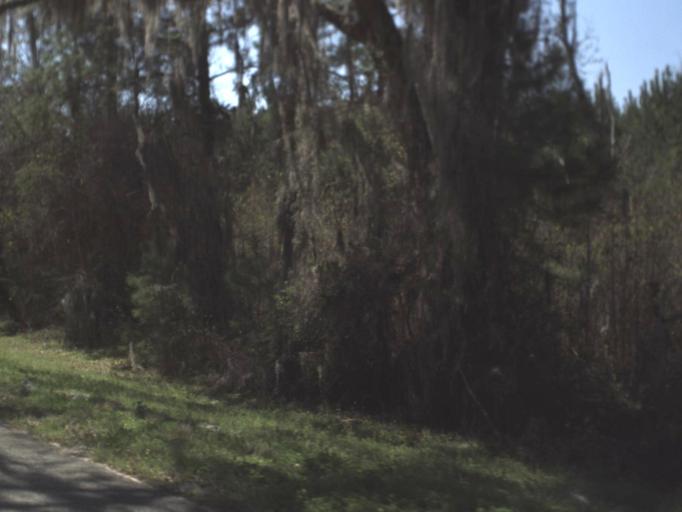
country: US
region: Florida
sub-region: Jefferson County
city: Monticello
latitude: 30.3926
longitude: -84.0133
